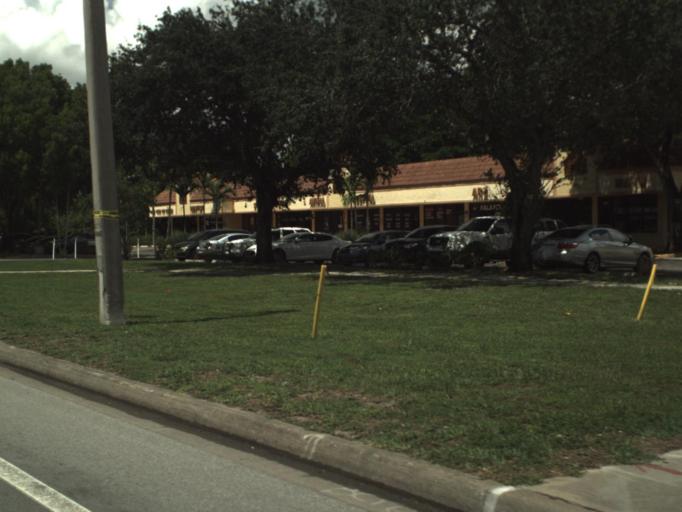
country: US
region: Florida
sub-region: Broward County
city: Parkland
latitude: 26.3128
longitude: -80.2022
